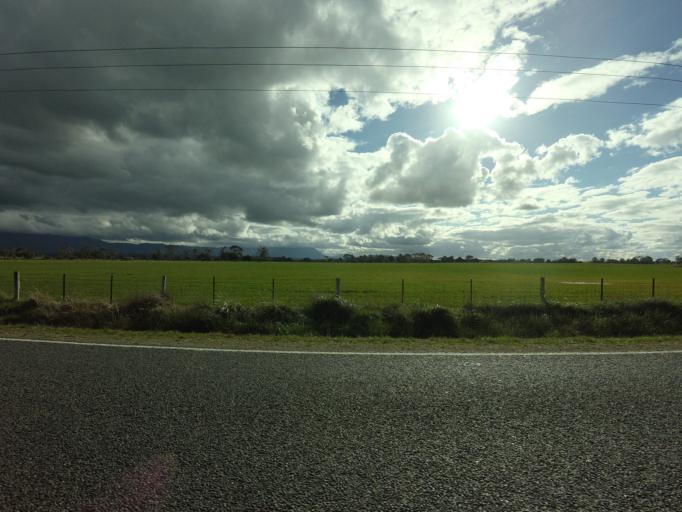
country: AU
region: Tasmania
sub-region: Northern Midlands
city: Longford
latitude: -41.7311
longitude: 147.0864
